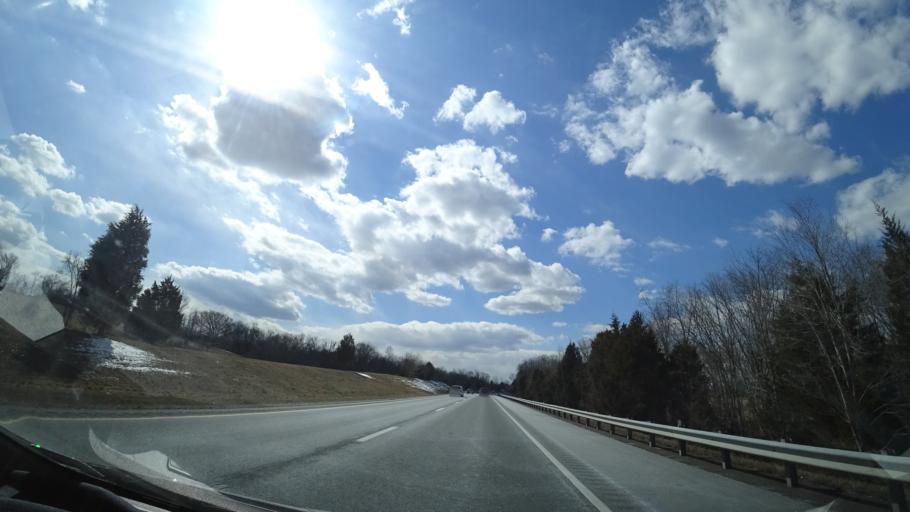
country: US
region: Virginia
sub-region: Fauquier County
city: Marshall
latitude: 38.8476
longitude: -77.7773
